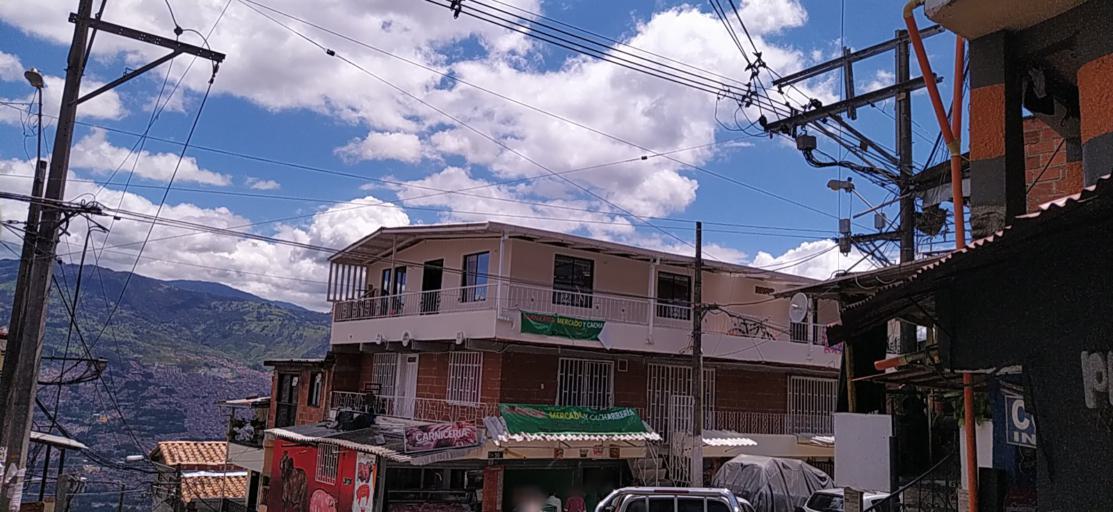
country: CO
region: Antioquia
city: Medellin
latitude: 6.2913
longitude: -75.5413
